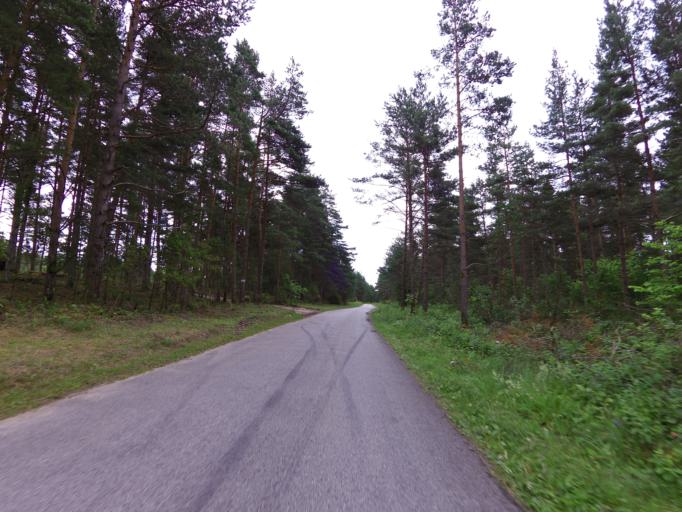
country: EE
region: Laeaene
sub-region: Vormsi vald
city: Hullo
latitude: 58.9784
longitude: 23.2550
